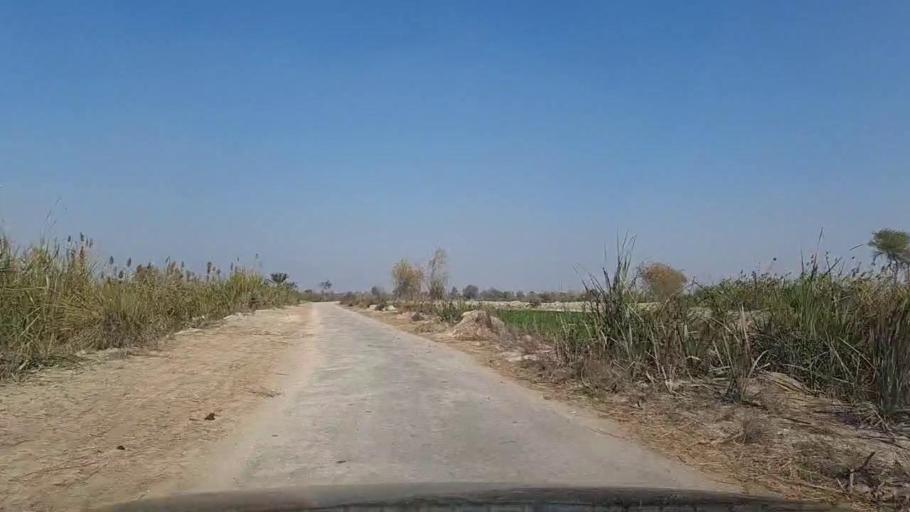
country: PK
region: Sindh
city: Bandhi
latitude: 26.5506
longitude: 68.3387
